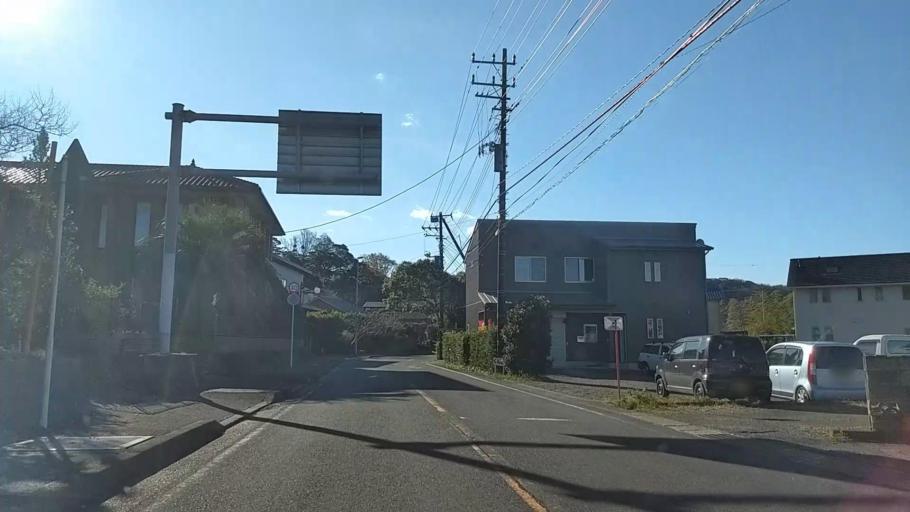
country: JP
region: Chiba
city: Futtsu
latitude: 35.2195
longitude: 139.8725
